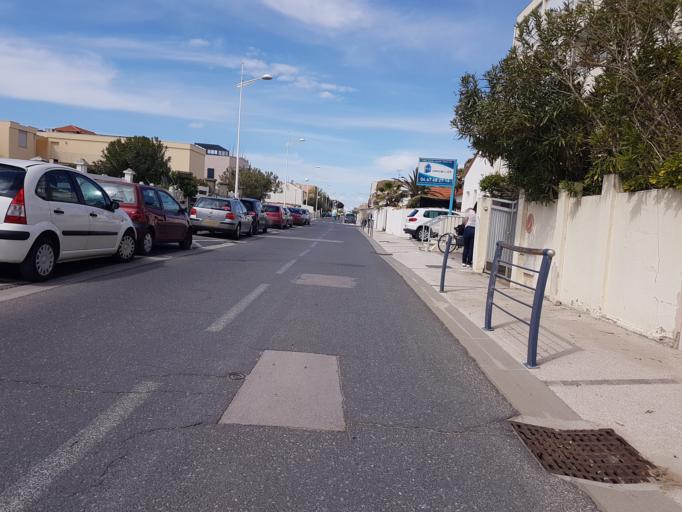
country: FR
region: Languedoc-Roussillon
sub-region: Departement de l'Herault
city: Perols
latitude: 43.5462
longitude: 3.9836
